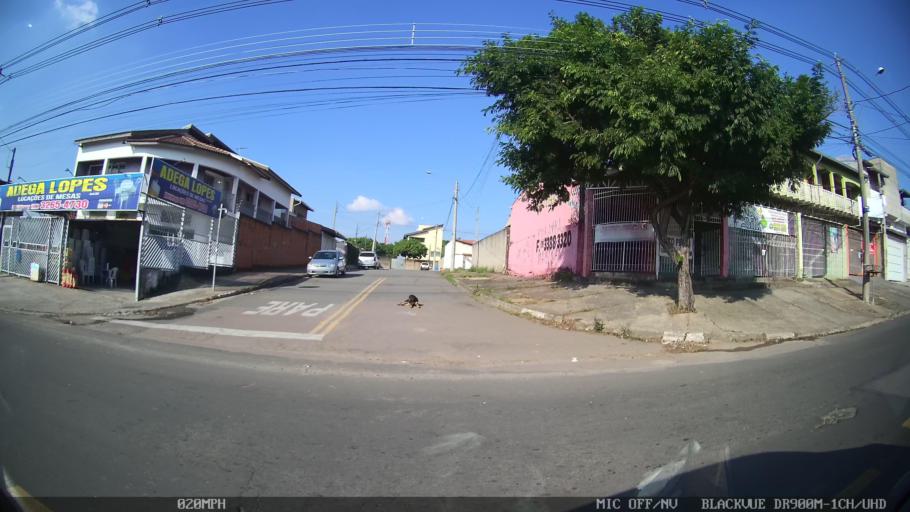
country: BR
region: Sao Paulo
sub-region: Campinas
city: Campinas
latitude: -22.9852
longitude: -47.1485
